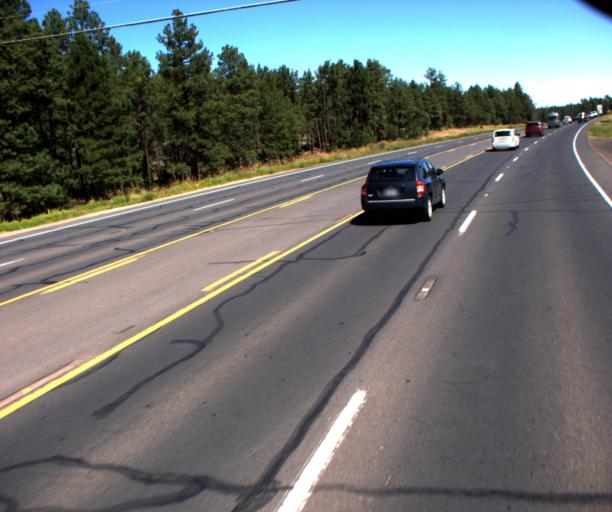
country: US
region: Arizona
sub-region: Navajo County
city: Show Low
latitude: 34.2152
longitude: -110.0286
